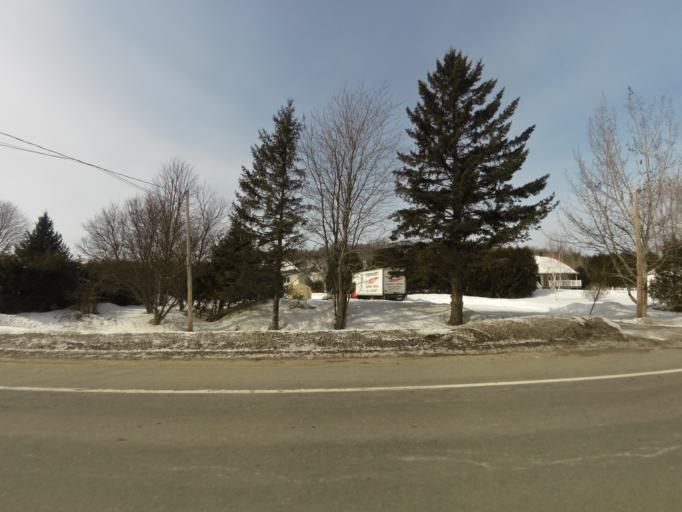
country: CA
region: Quebec
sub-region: Laurentides
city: Mont-Laurier
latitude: 46.5662
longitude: -75.4888
